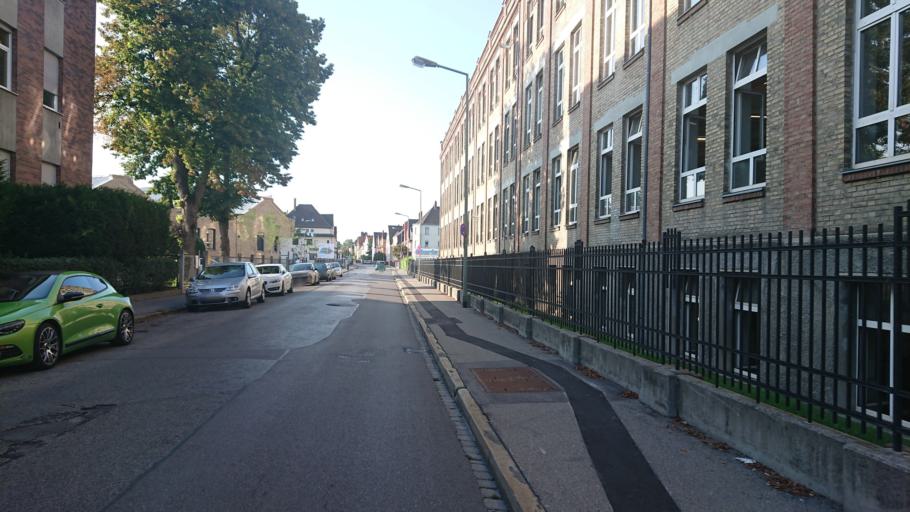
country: DE
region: Bavaria
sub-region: Swabia
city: Augsburg
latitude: 48.3672
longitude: 10.8732
